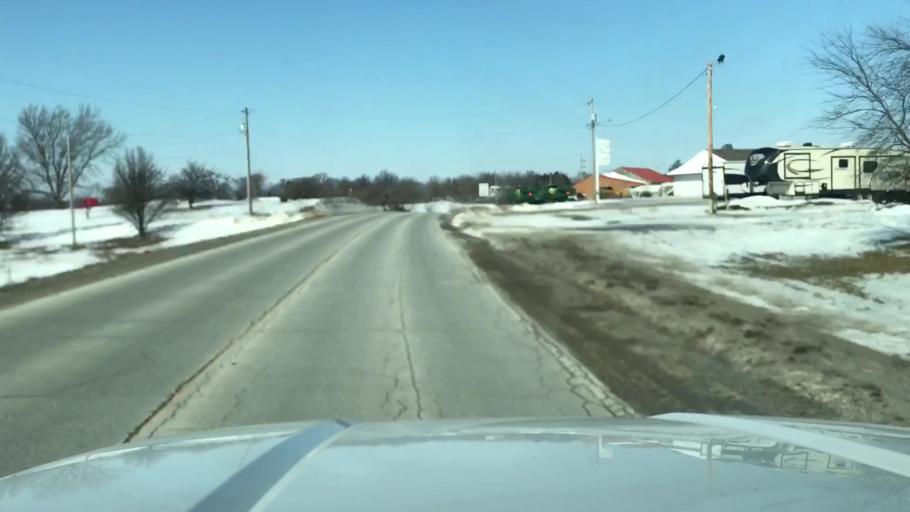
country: US
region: Missouri
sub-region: Andrew County
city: Savannah
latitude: 39.9501
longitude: -94.8447
